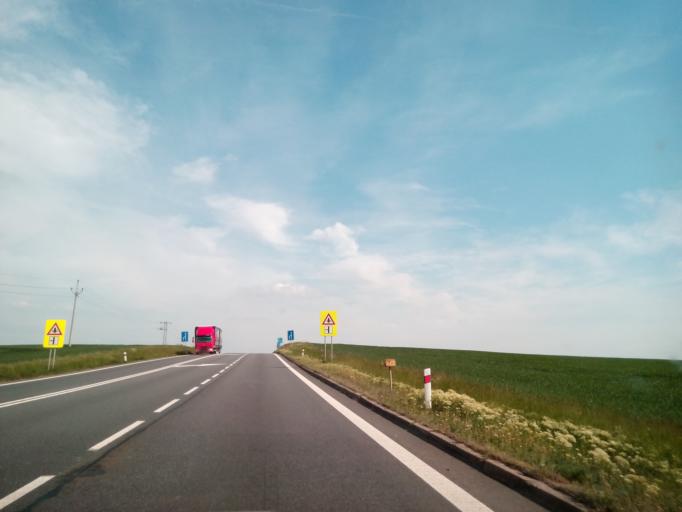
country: CZ
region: South Moravian
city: Krenovice
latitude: 49.1693
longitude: 16.8387
